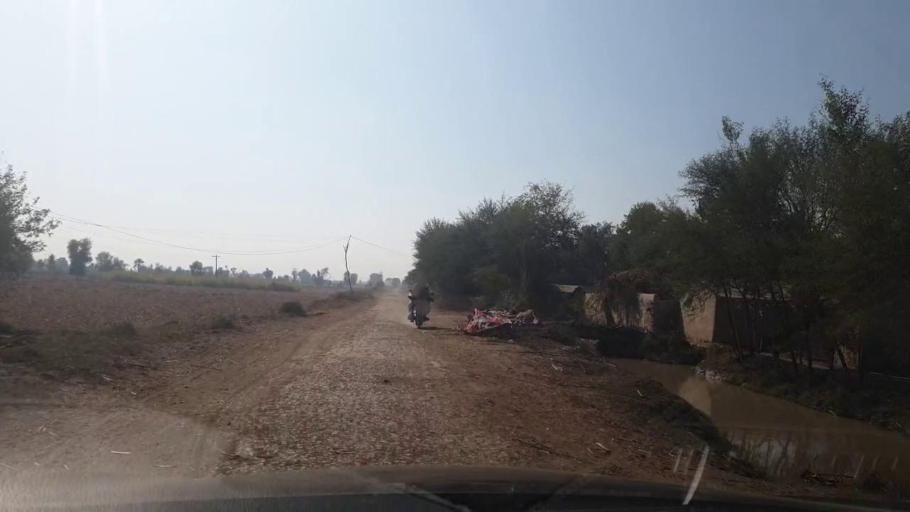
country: PK
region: Sindh
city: Ubauro
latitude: 28.1516
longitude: 69.6931
